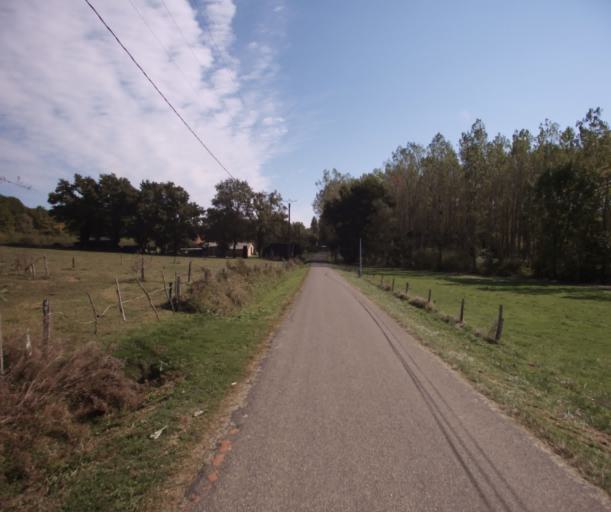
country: FR
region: Midi-Pyrenees
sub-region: Departement du Gers
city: Cazaubon
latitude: 43.9479
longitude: -0.0635
